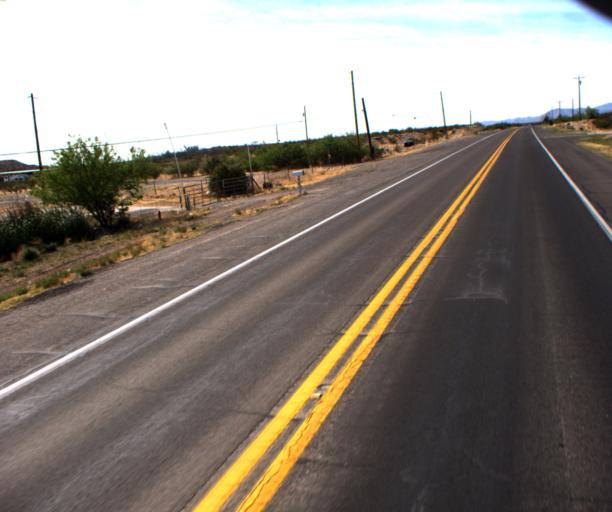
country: US
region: Arizona
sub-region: Graham County
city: Cactus Flat
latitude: 32.7567
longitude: -109.7163
